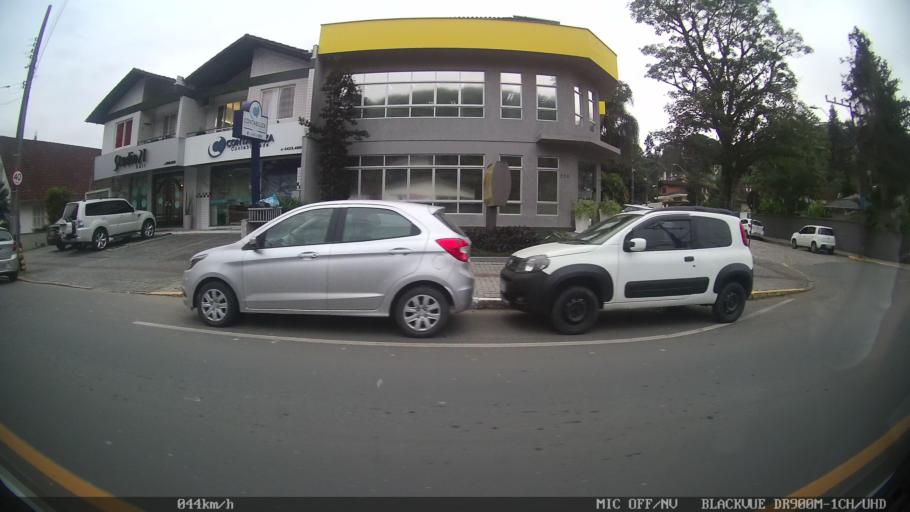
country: BR
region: Santa Catarina
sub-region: Joinville
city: Joinville
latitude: -26.3029
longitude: -48.8580
